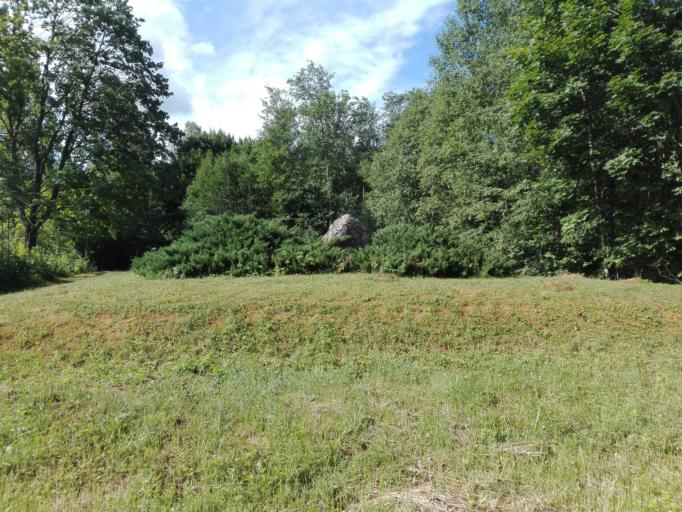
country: LT
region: Panevezys
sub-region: Birzai
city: Birzai
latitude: 56.2245
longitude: 24.7808
